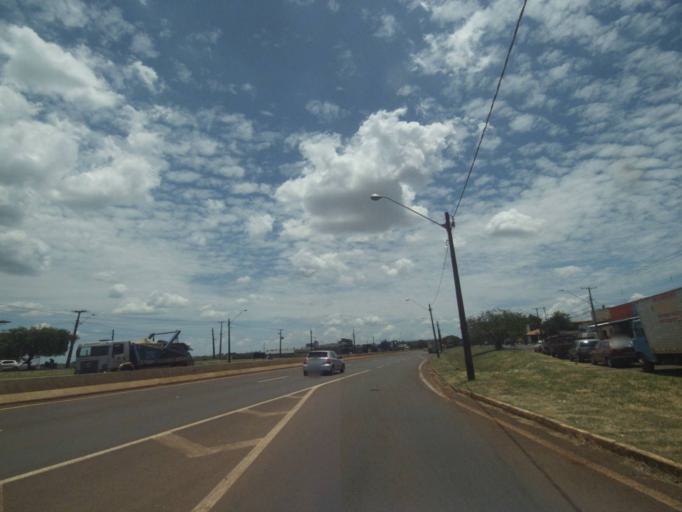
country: BR
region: Parana
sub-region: Londrina
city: Londrina
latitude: -23.3658
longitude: -51.1436
